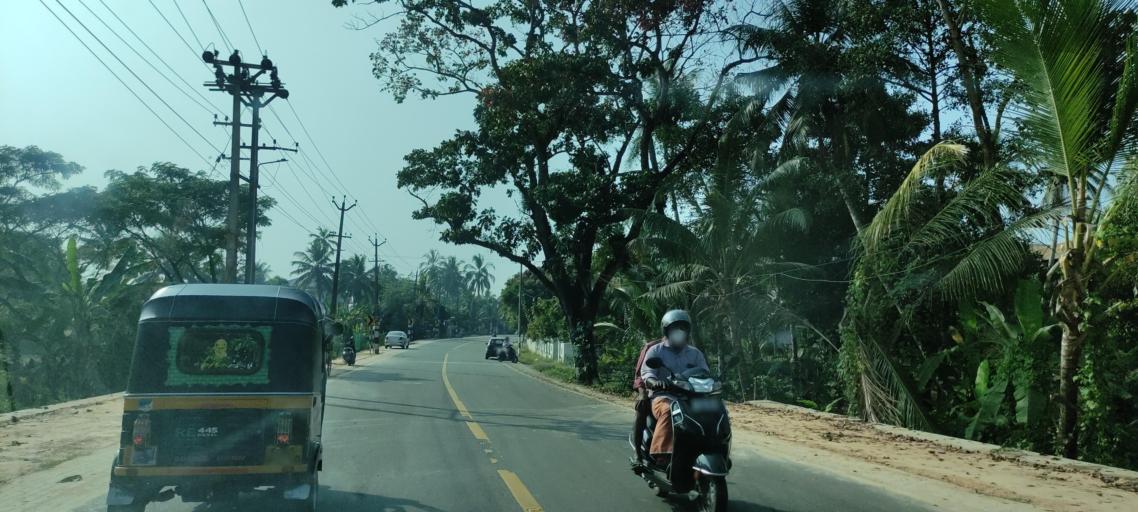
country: IN
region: Kerala
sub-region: Kottayam
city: Changanacheri
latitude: 9.3630
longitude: 76.4480
